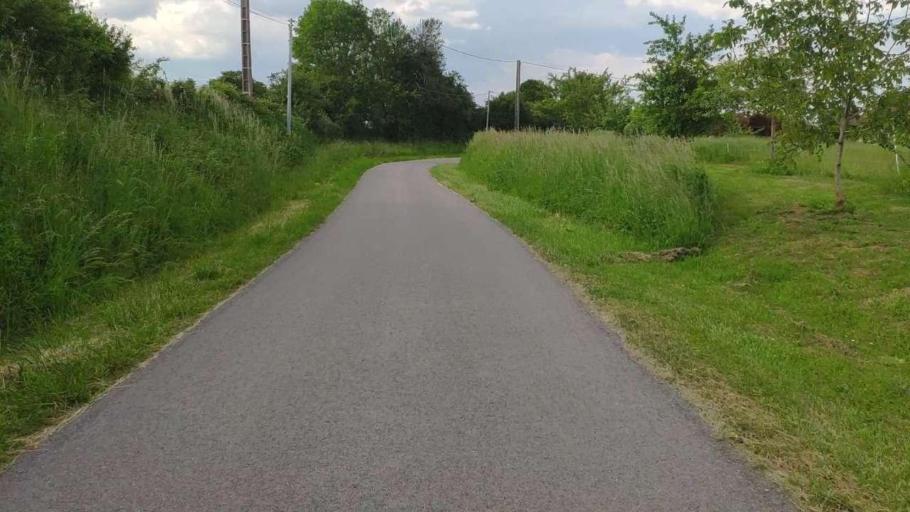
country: FR
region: Franche-Comte
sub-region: Departement du Jura
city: Bletterans
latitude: 46.7959
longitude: 5.3649
